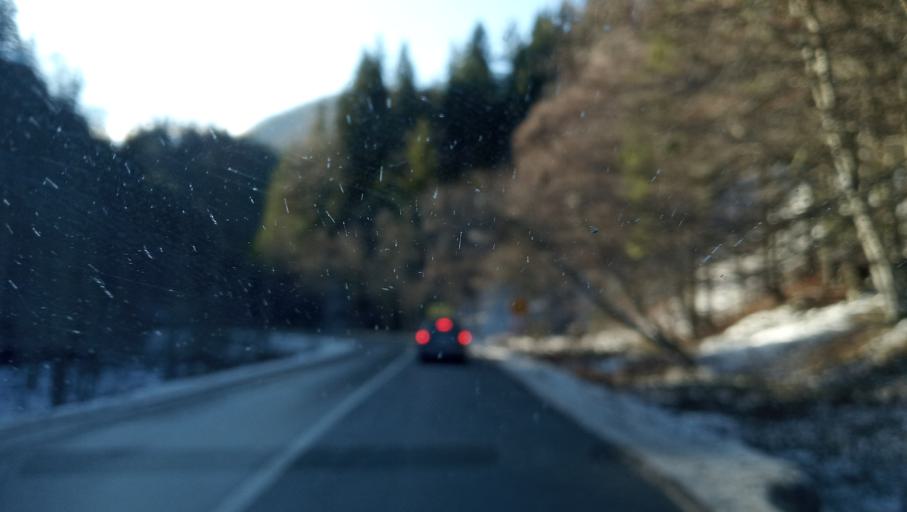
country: RO
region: Brasov
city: Crivina
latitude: 45.4781
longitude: 25.9197
